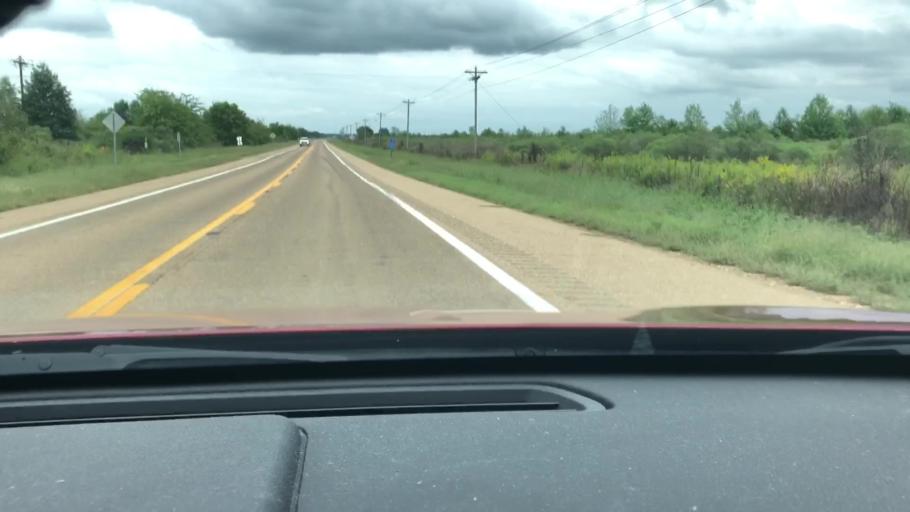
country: US
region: Arkansas
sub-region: Miller County
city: Texarkana
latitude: 33.4127
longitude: -93.8055
